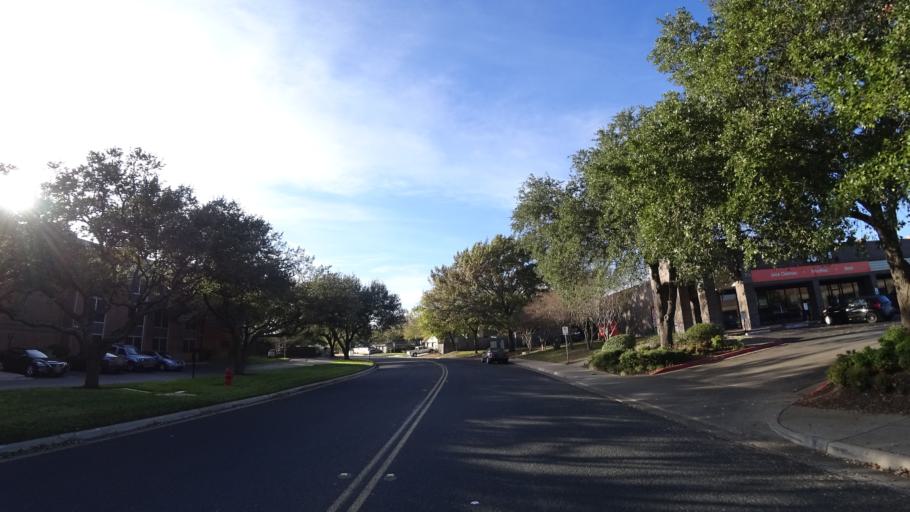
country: US
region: Texas
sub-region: Williamson County
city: Jollyville
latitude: 30.3688
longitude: -97.7290
